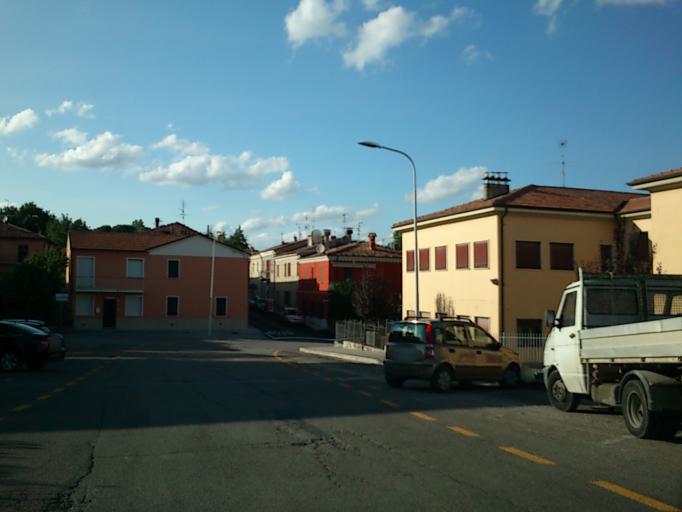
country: IT
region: The Marches
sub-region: Provincia di Pesaro e Urbino
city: Urbania
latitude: 43.6665
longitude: 12.5199
